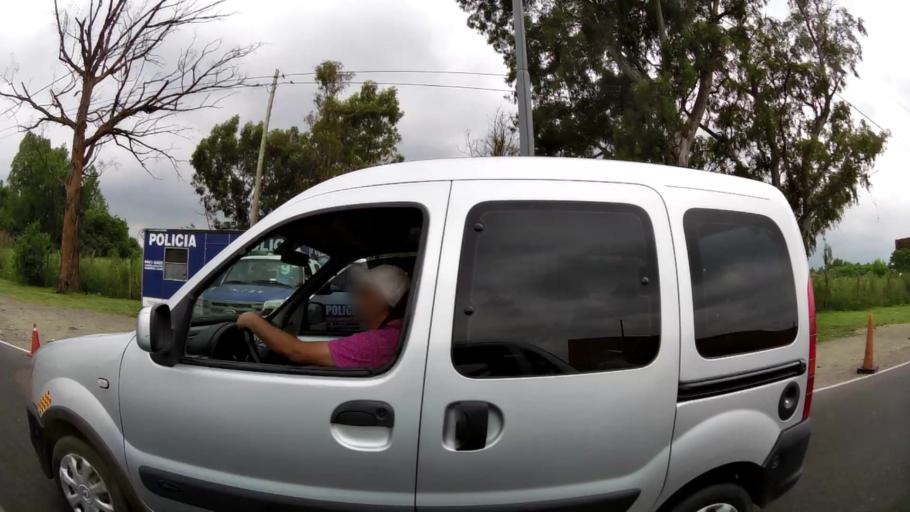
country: AR
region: Buenos Aires
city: San Justo
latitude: -34.7060
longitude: -58.5333
